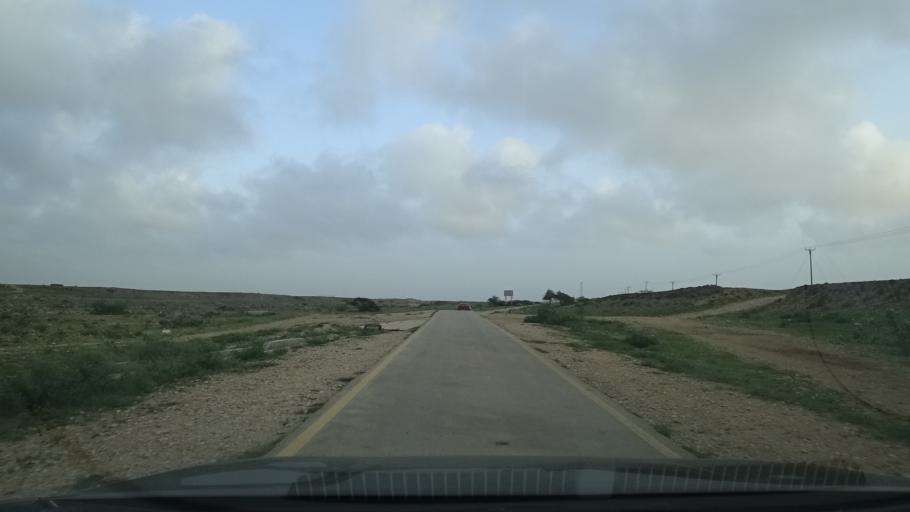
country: OM
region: Zufar
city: Salalah
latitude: 17.0960
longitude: 54.2331
